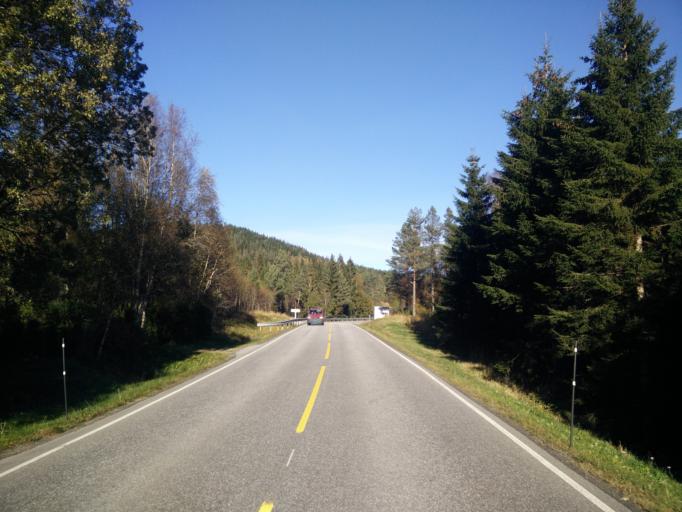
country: NO
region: More og Romsdal
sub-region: Tingvoll
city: Tingvoll
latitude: 63.0333
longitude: 8.0320
